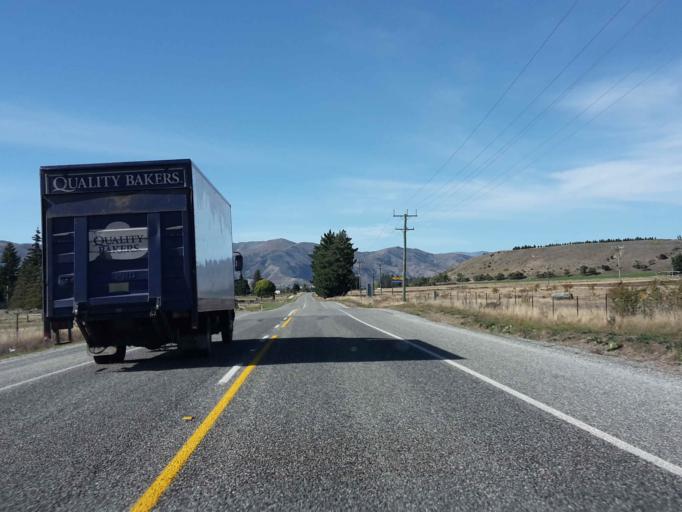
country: NZ
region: Otago
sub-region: Queenstown-Lakes District
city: Wanaka
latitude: -44.7202
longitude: 169.2267
